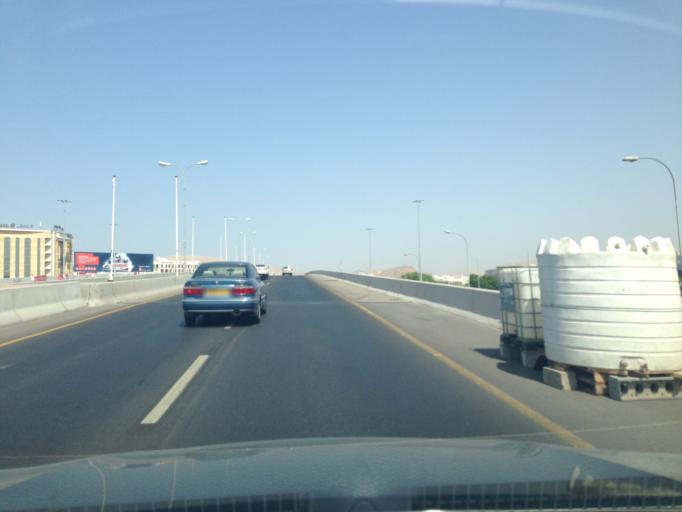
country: OM
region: Muhafazat Masqat
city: Muscat
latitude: 23.6128
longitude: 58.4899
